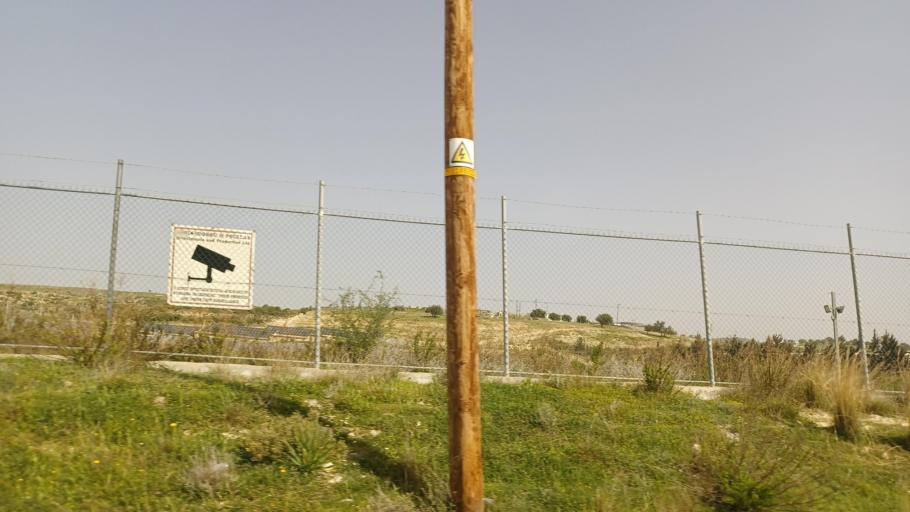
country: CY
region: Limassol
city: Pissouri
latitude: 34.6853
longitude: 32.7038
